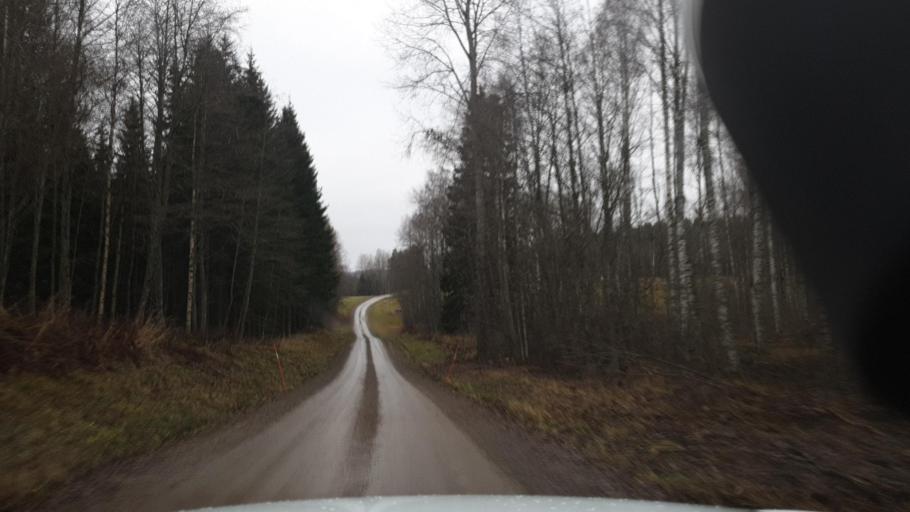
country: SE
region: Vaermland
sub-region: Eda Kommun
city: Amotfors
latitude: 59.8113
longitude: 12.3617
